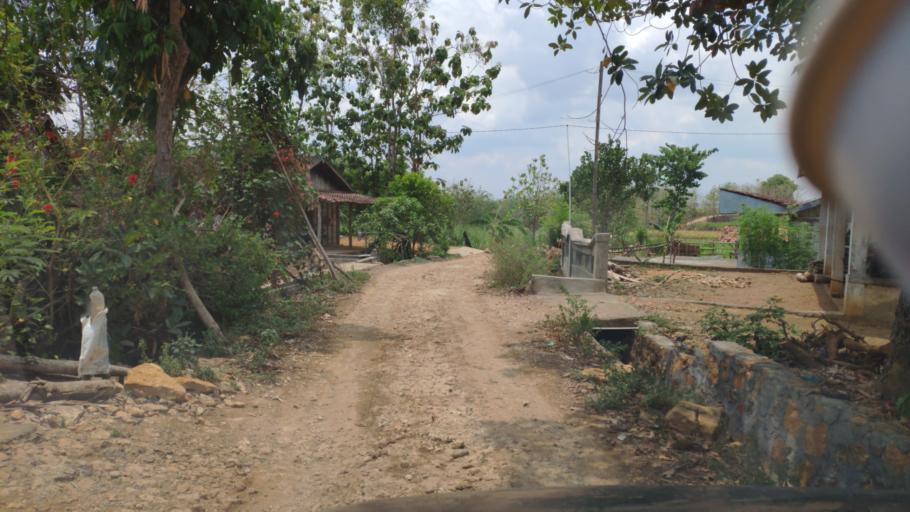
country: ID
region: Central Java
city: Ngapus
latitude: -6.9674
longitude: 111.2228
